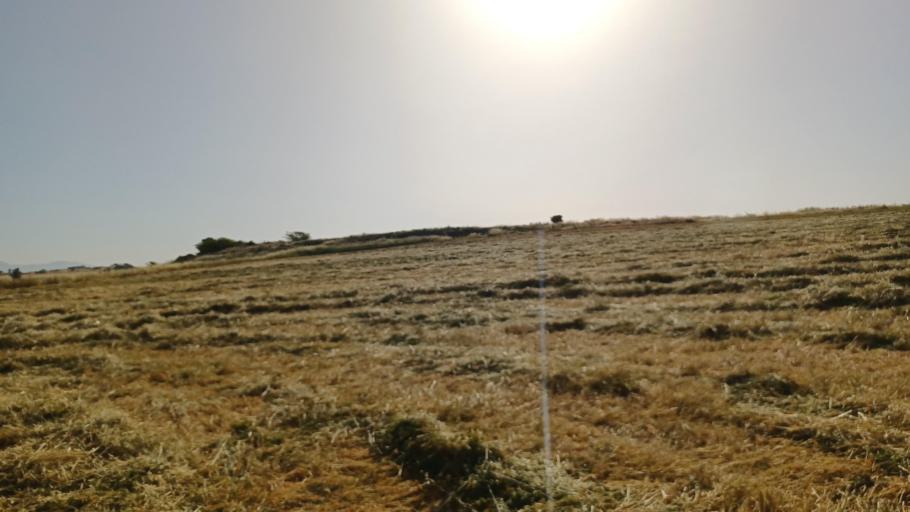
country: CY
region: Lefkosia
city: Mammari
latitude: 35.1653
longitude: 33.2452
